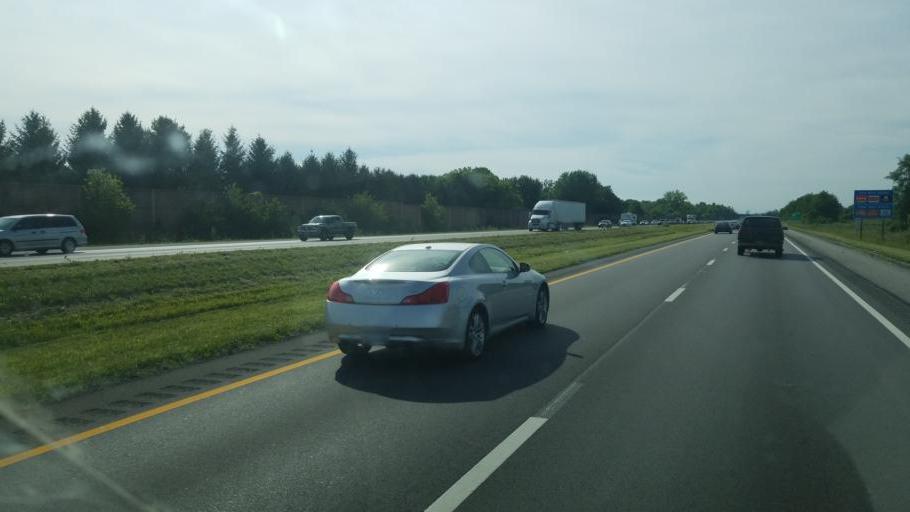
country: US
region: Ohio
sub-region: Franklin County
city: Groveport
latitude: 39.8781
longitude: -82.8655
